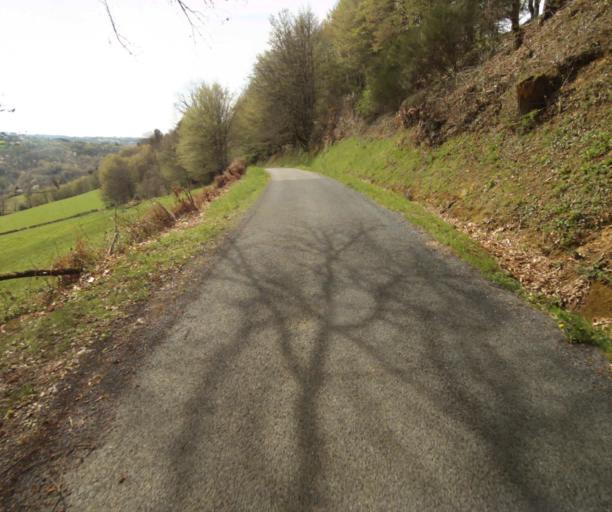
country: FR
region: Limousin
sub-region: Departement de la Correze
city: Laguenne
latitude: 45.2571
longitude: 1.8164
